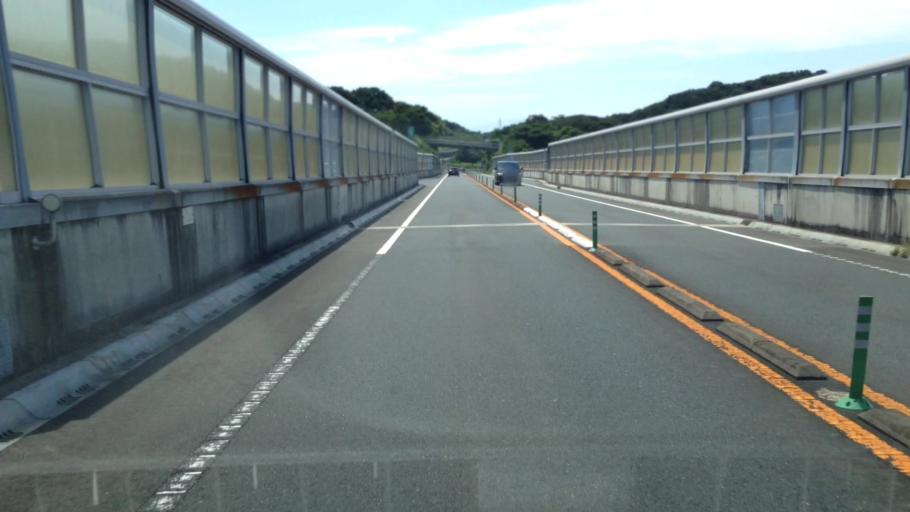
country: JP
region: Kanagawa
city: Yokosuka
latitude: 35.2322
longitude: 139.6484
